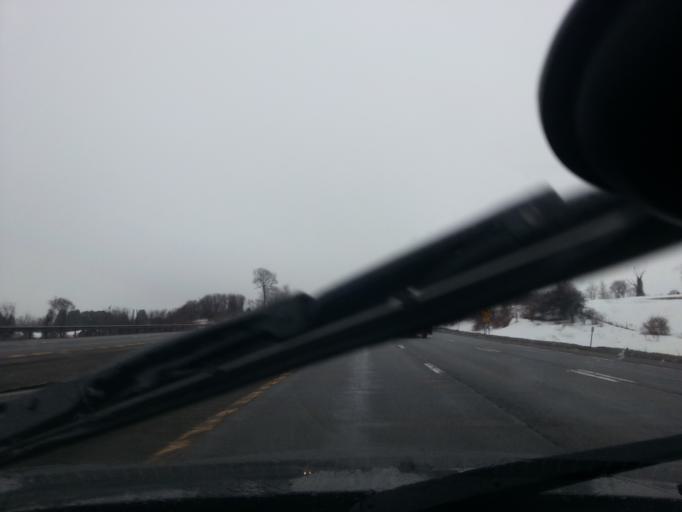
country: US
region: New York
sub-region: Onondaga County
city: Nedrow
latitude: 42.8860
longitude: -76.1097
